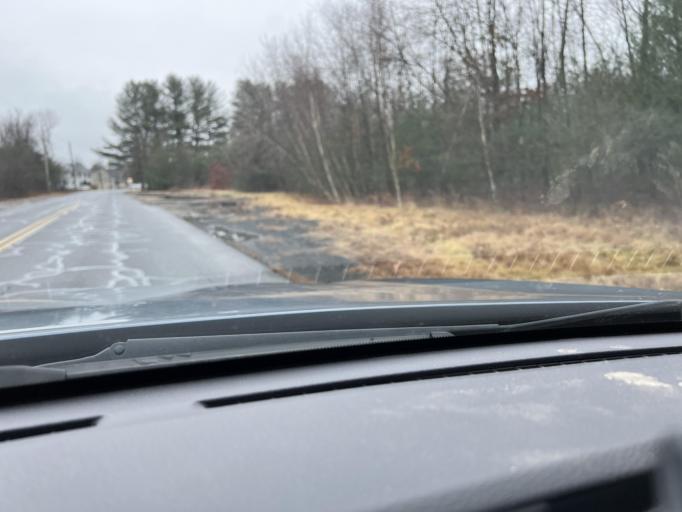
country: US
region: Connecticut
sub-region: Hartford County
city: Suffield Depot
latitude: 42.0413
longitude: -72.6944
